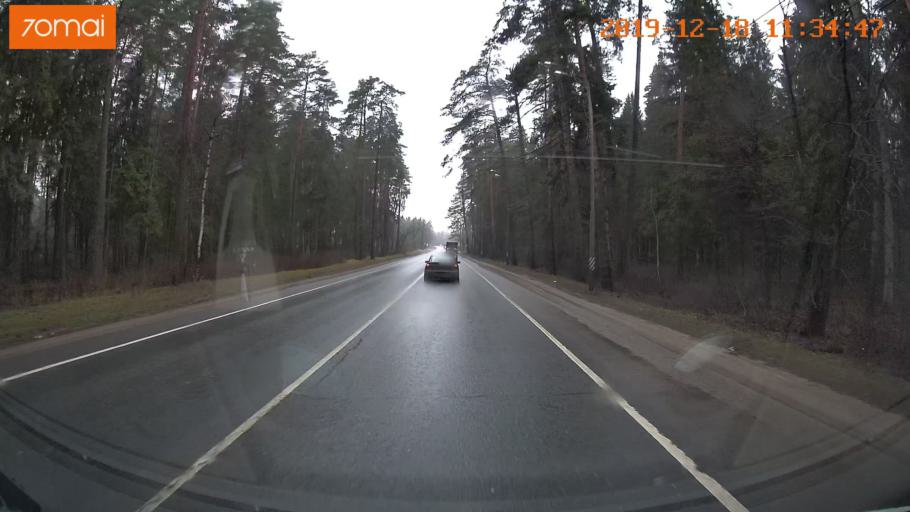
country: RU
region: Moskovskaya
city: Bol'shiye Vyazemy
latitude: 55.6766
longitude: 36.9287
